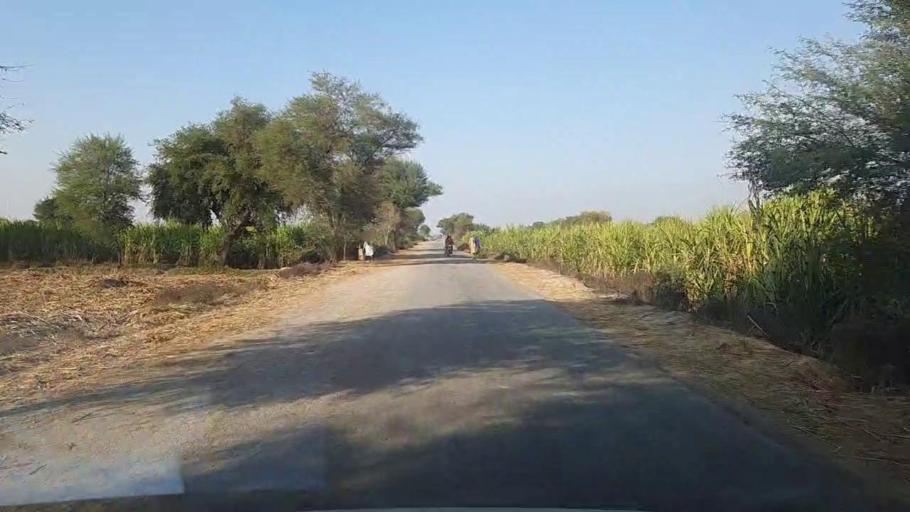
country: PK
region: Sindh
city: Phulji
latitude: 26.8495
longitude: 67.7937
